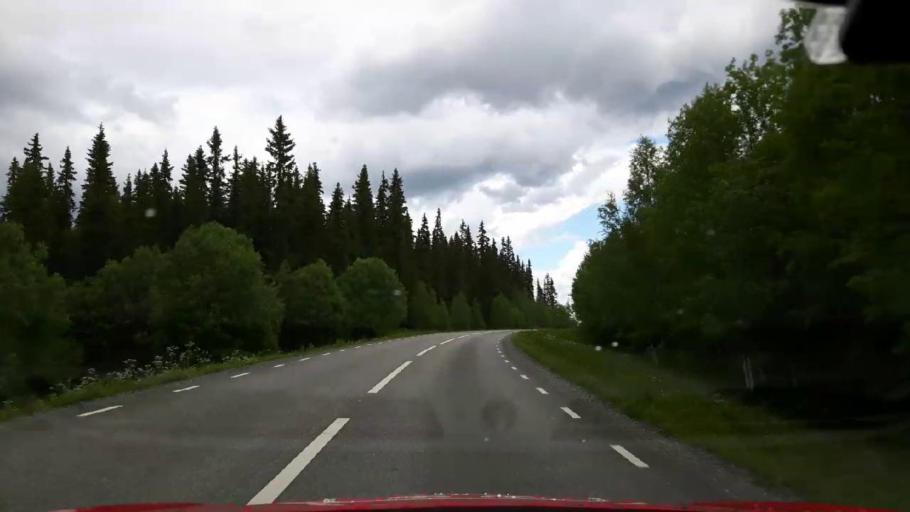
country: SE
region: Jaemtland
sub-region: Krokoms Kommun
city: Krokom
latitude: 63.7812
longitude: 14.3503
